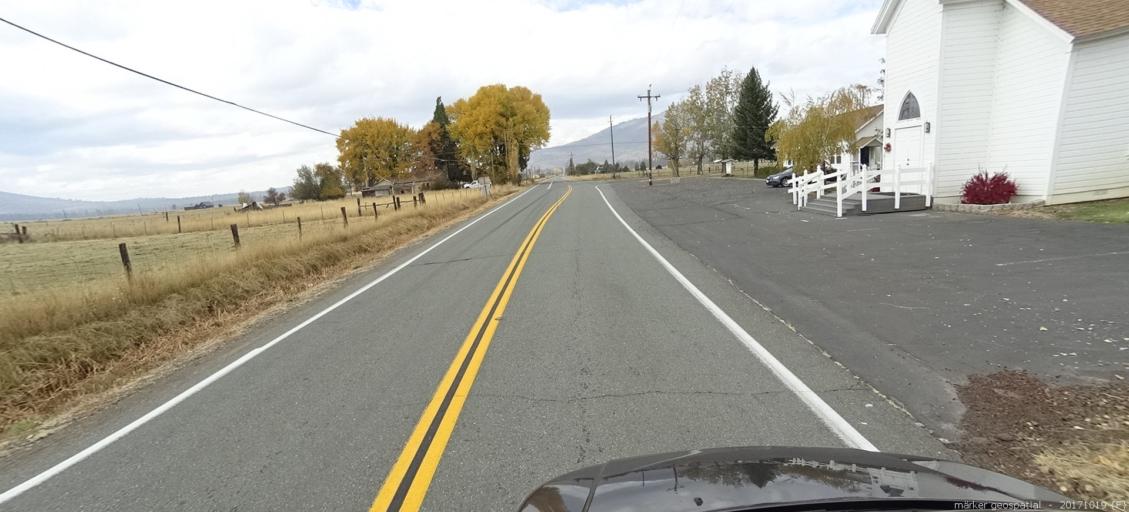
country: US
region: California
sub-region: Shasta County
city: Burney
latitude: 41.0616
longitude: -121.4886
